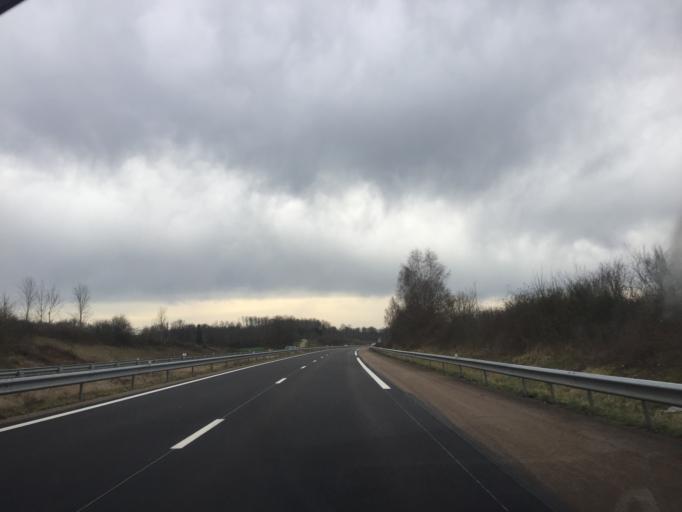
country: FR
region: Franche-Comte
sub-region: Departement du Jura
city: Montmorot
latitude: 46.7281
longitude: 5.5068
